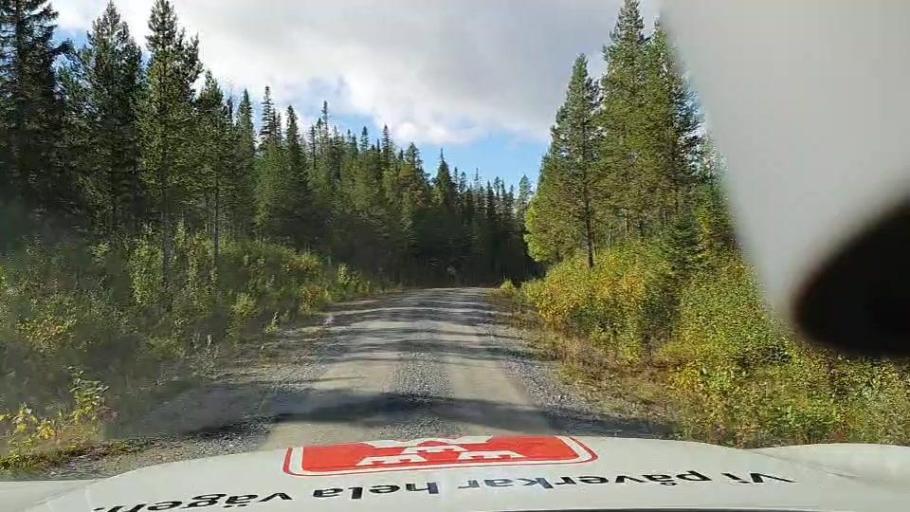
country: SE
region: Jaemtland
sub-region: Are Kommun
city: Jarpen
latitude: 63.1791
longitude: 13.6141
